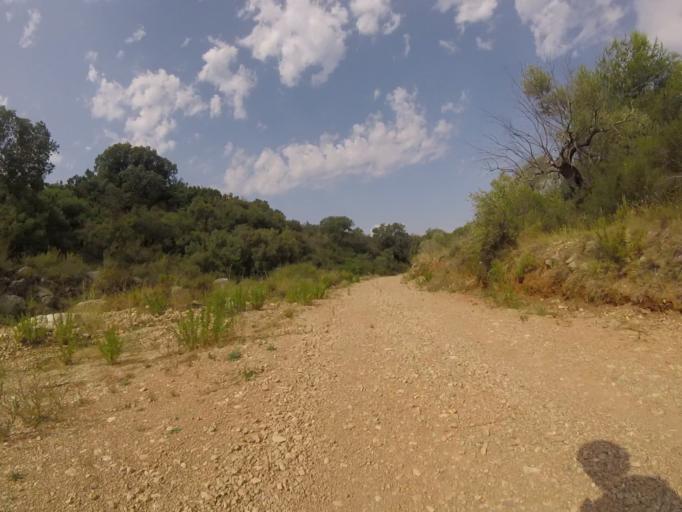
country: ES
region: Valencia
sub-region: Provincia de Castello
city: Alcala de Xivert
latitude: 40.3349
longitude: 0.1976
